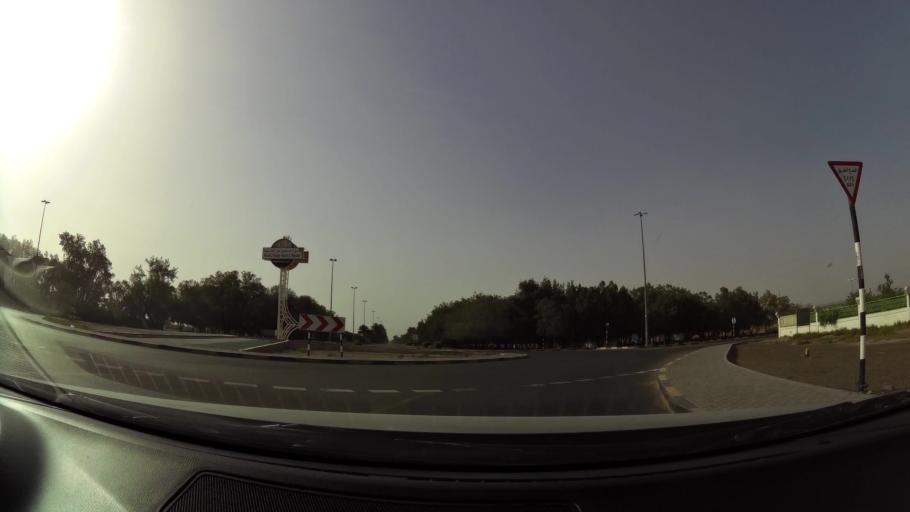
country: AE
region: Abu Dhabi
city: Al Ain
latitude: 24.0906
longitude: 55.7241
